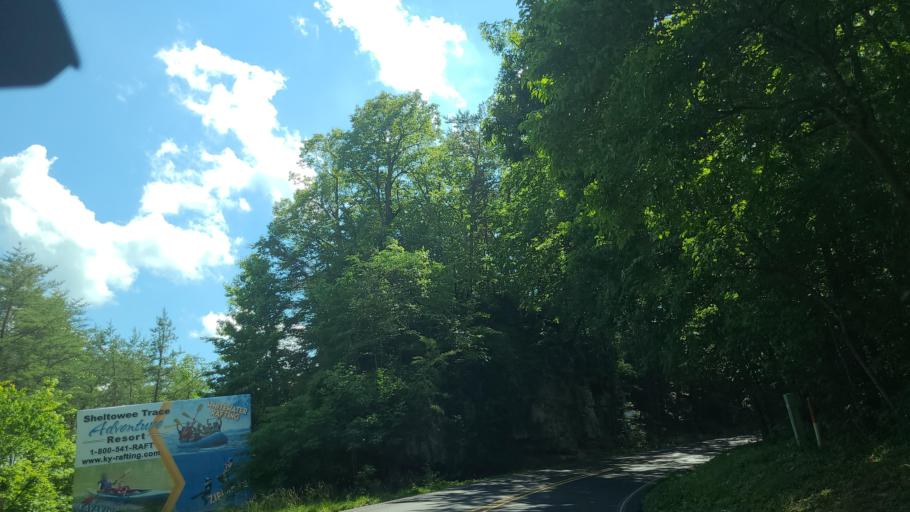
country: US
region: Kentucky
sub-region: McCreary County
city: Whitley City
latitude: 36.8431
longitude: -84.3233
